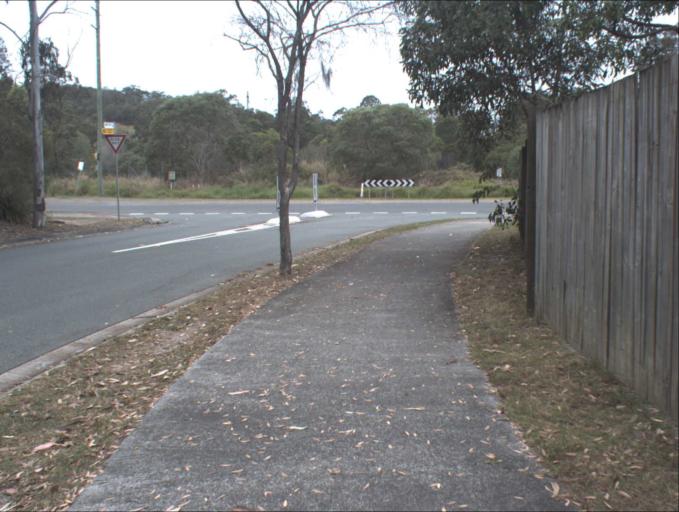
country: AU
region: Queensland
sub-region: Logan
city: Beenleigh
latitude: -27.6639
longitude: 153.2092
